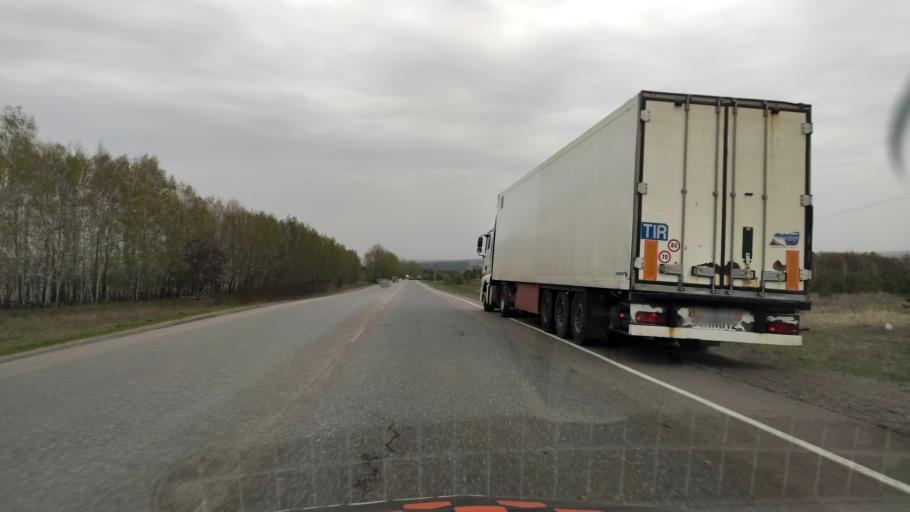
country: RU
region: Kursk
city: Gorshechnoye
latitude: 51.4584
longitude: 37.9221
